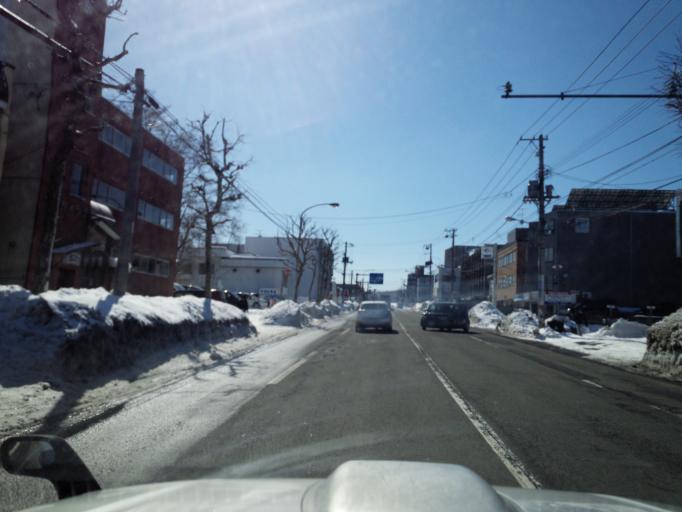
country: JP
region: Hokkaido
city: Sapporo
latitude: 43.0040
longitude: 141.4302
